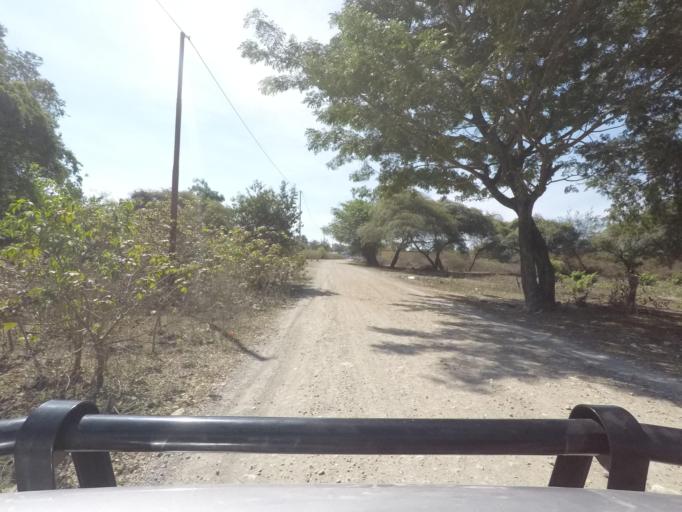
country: TL
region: Bobonaro
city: Maliana
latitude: -8.8917
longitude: 125.0036
